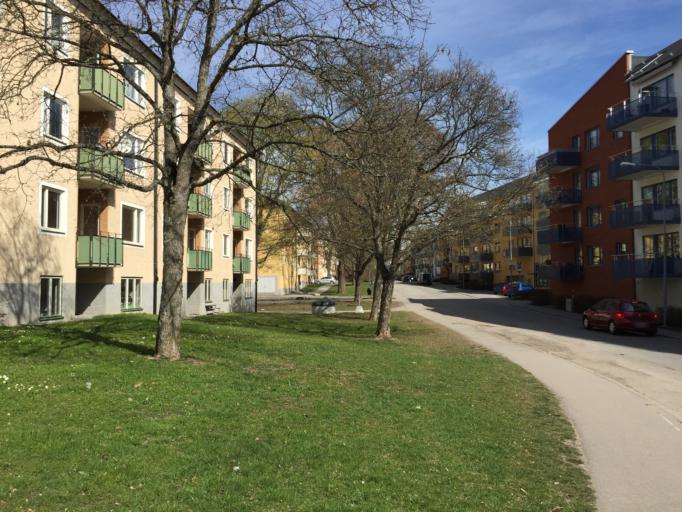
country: SE
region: Stockholm
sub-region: Stockholms Kommun
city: Bromma
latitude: 59.3564
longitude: 17.8865
